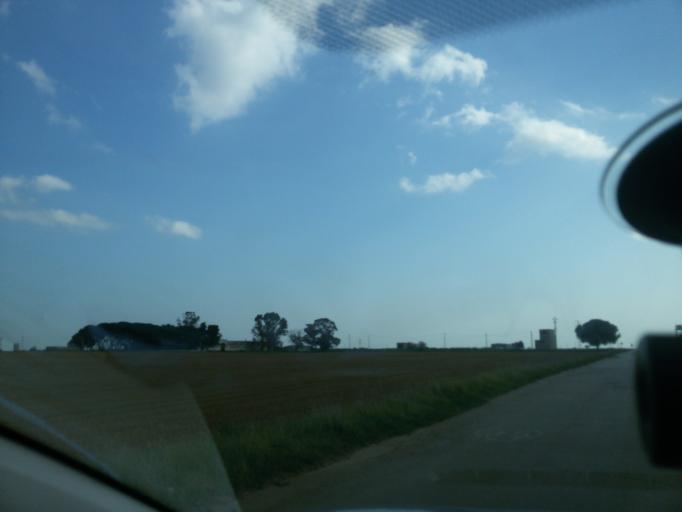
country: IT
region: Apulia
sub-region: Provincia di Brindisi
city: Mesagne
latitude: 40.6466
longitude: 17.8154
